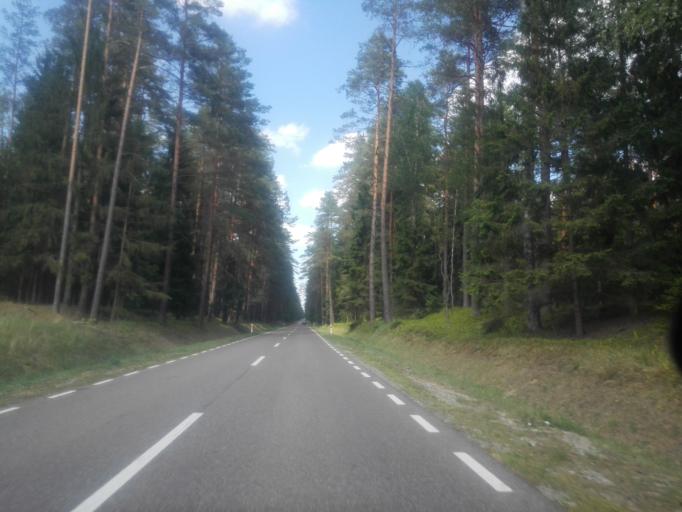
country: PL
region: Podlasie
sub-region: Powiat augustowski
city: Augustow
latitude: 53.9113
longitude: 23.1414
